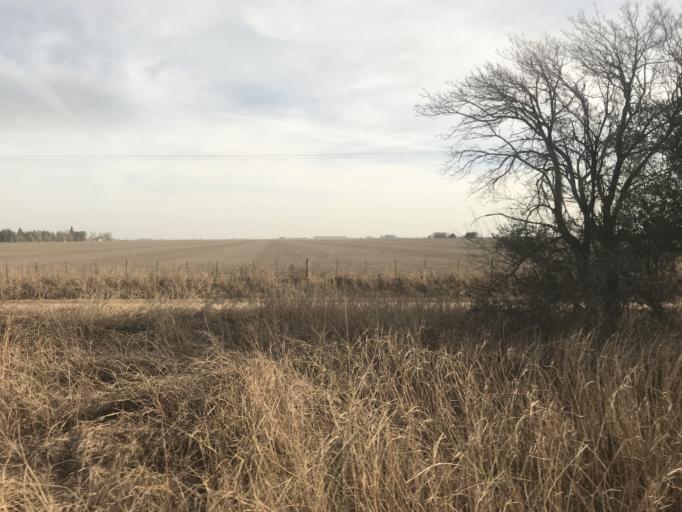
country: AR
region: Cordoba
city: Pilar
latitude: -31.7074
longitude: -63.8637
